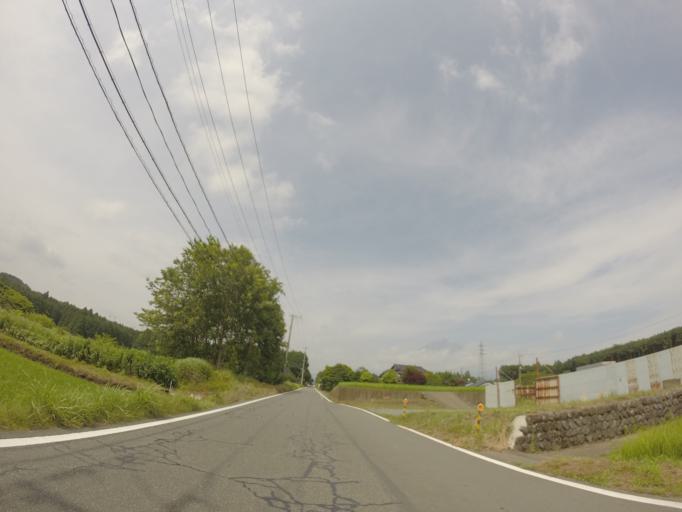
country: JP
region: Shizuoka
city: Fujinomiya
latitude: 35.2936
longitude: 138.5825
